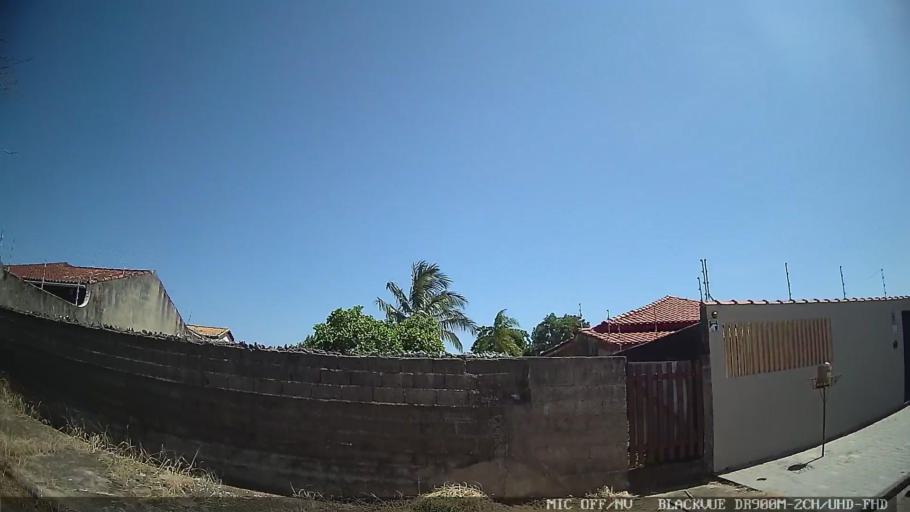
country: BR
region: Sao Paulo
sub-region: Peruibe
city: Peruibe
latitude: -24.2988
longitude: -46.9788
